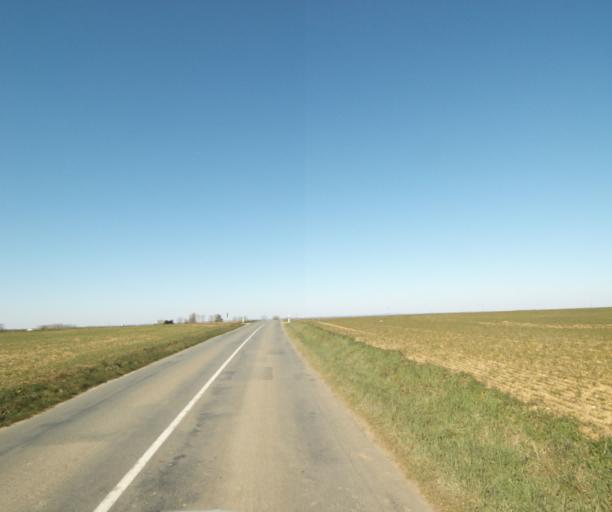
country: FR
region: Poitou-Charentes
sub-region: Departement des Deux-Sevres
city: Saint-Maxire
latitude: 46.3687
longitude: -0.4920
